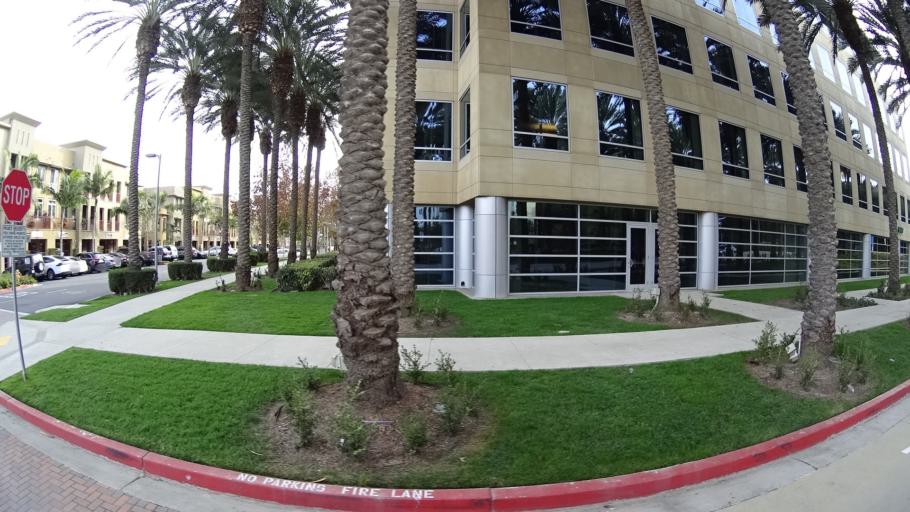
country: US
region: California
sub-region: Orange County
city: Aliso Viejo
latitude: 33.5795
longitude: -117.7296
